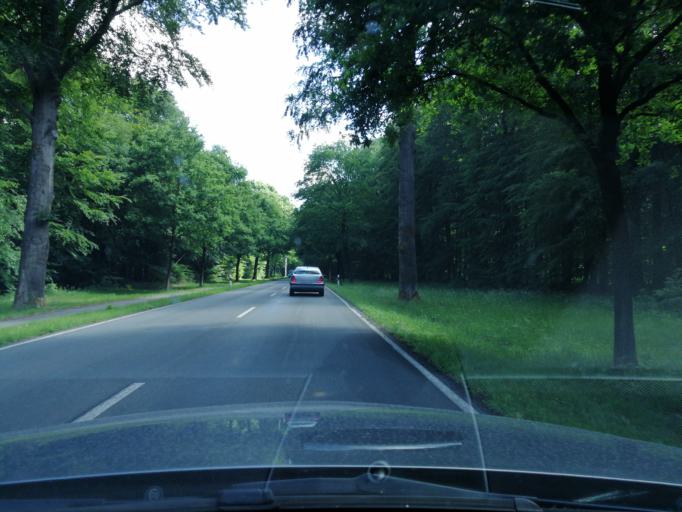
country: DE
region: North Rhine-Westphalia
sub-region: Regierungsbezirk Dusseldorf
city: Kranenburg
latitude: 51.7300
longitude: 6.0679
